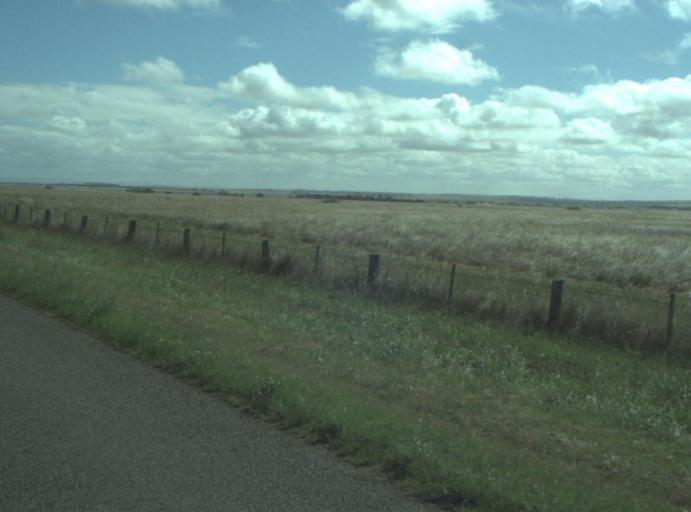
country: AU
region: Victoria
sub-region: Greater Geelong
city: Lara
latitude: -37.9441
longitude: 144.3092
